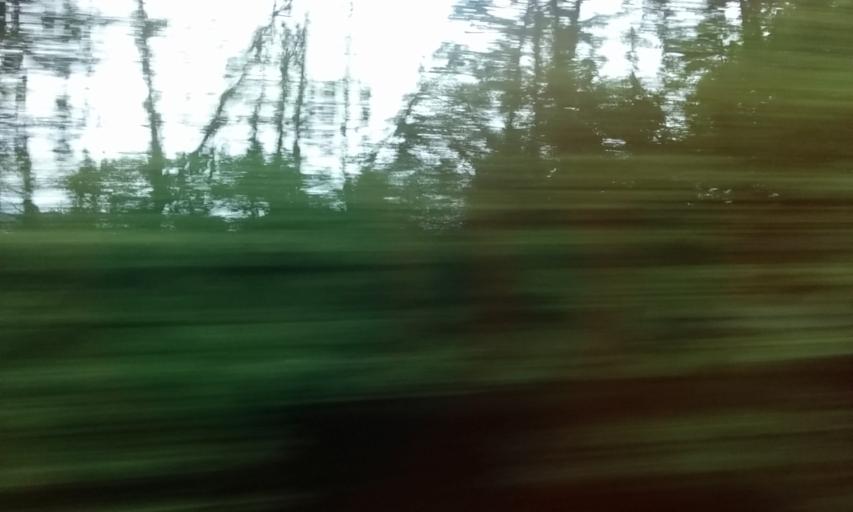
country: JP
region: Tochigi
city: Imaichi
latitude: 36.6805
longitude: 139.7109
